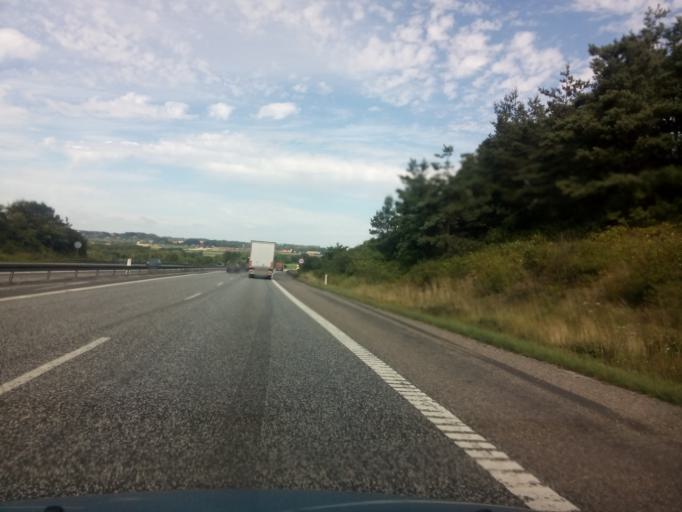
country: DK
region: Central Jutland
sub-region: Randers Kommune
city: Randers
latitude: 56.4433
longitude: 10.0097
